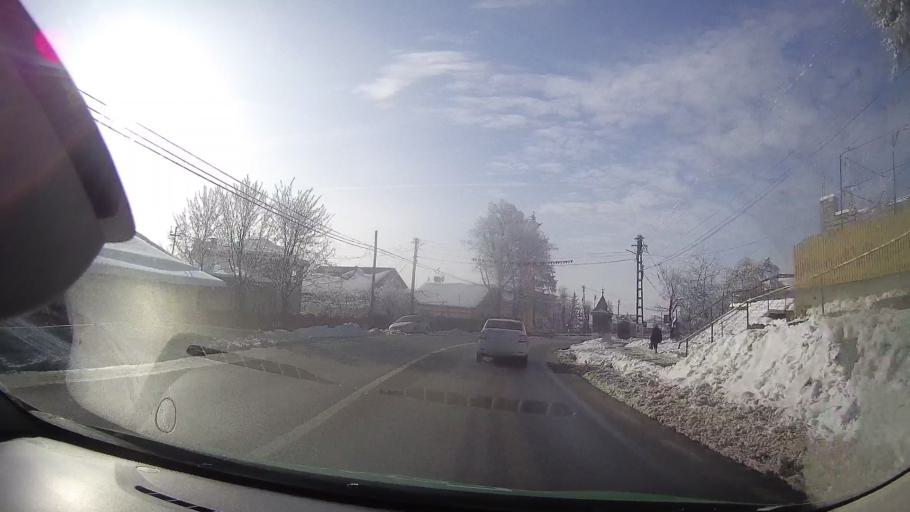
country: RO
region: Iasi
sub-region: Comuna Motca
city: Motca
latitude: 47.2353
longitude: 26.6031
